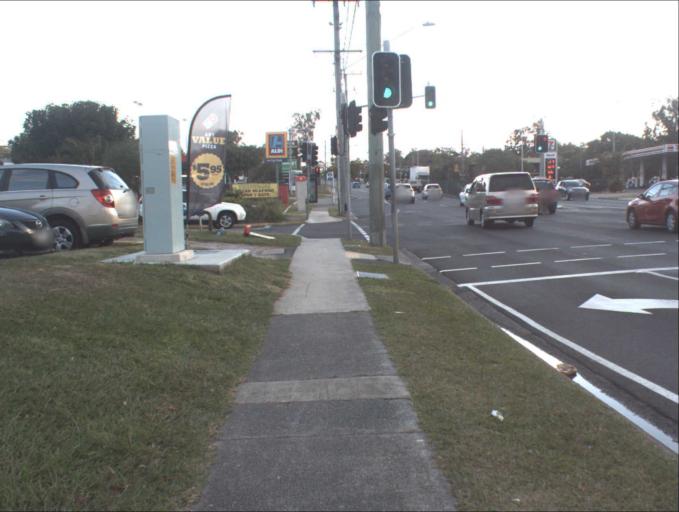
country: AU
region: Queensland
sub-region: Logan
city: Logan City
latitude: -27.6439
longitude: 153.1187
